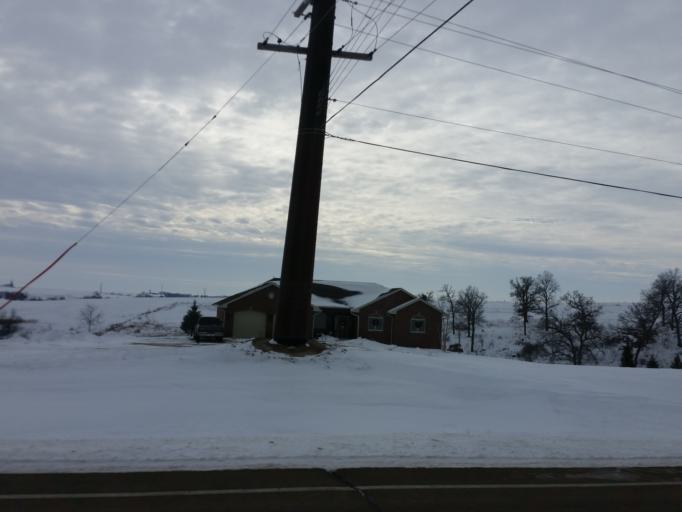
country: US
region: Iowa
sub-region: Dubuque County
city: Asbury
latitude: 42.3821
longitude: -90.7336
